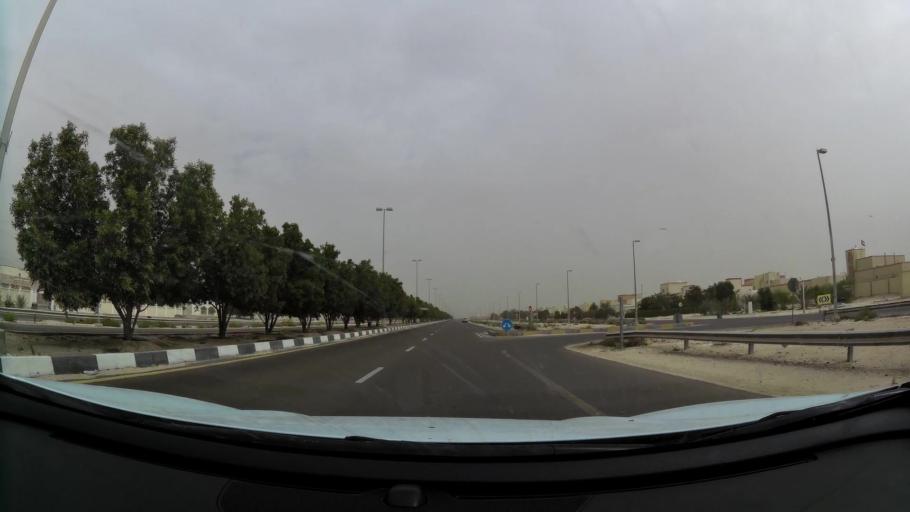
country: AE
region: Abu Dhabi
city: Abu Dhabi
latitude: 24.3784
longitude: 54.7188
